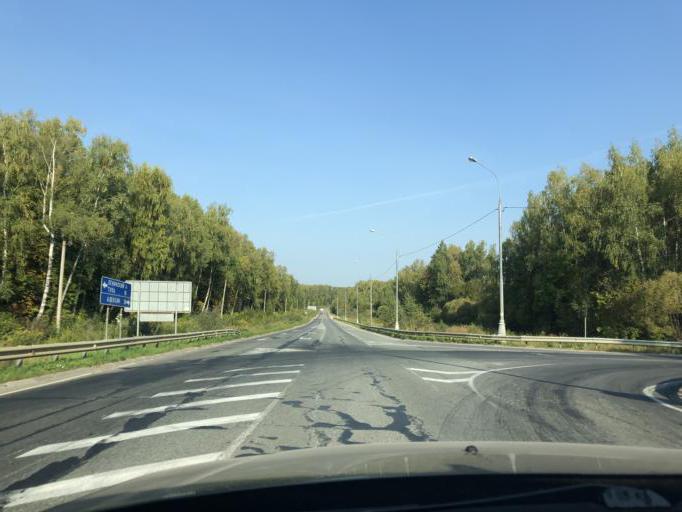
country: RU
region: Tula
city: Leninskiy
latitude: 54.3201
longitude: 37.4038
